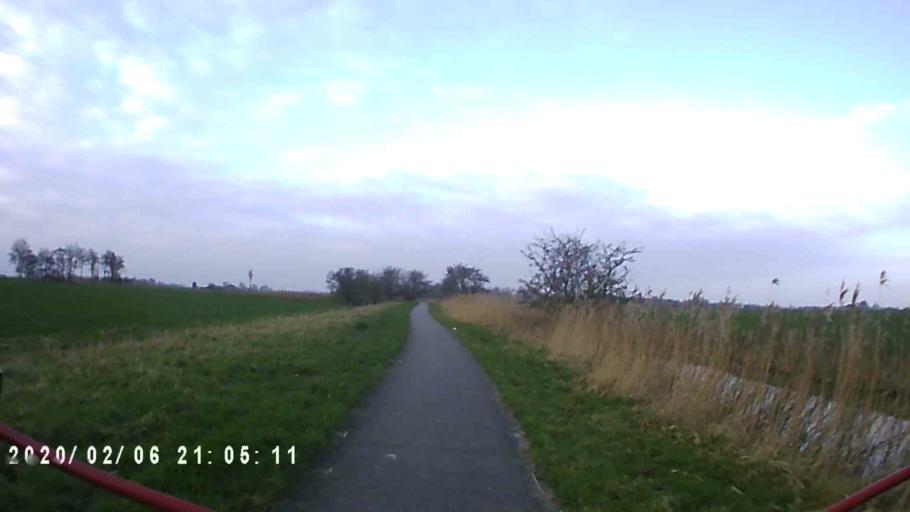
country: NL
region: Groningen
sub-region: Gemeente Zuidhorn
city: Oldehove
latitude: 53.3050
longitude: 6.4128
